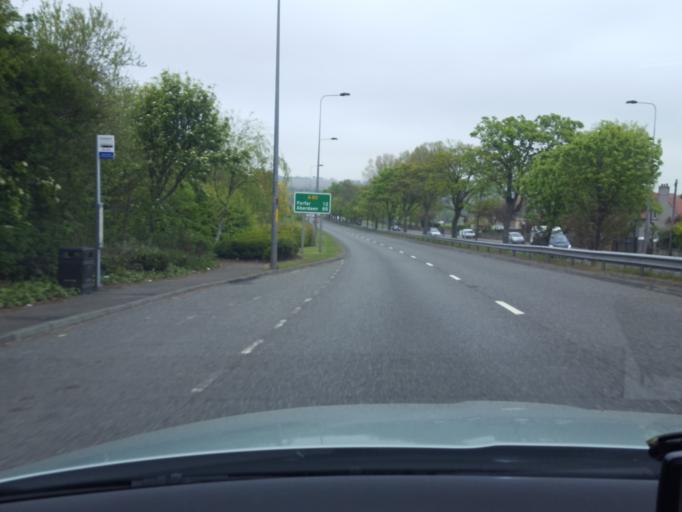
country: GB
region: Scotland
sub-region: Dundee City
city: Dundee
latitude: 56.4812
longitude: -2.9524
